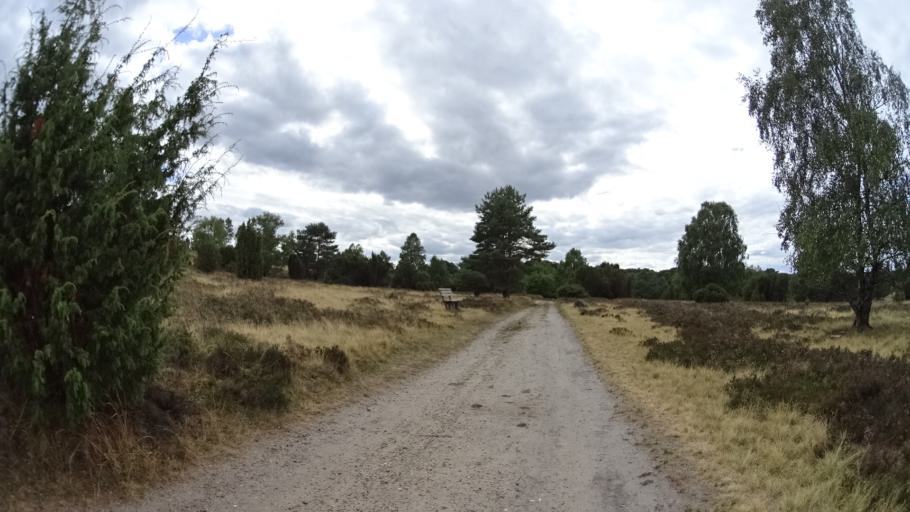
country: DE
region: Lower Saxony
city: Undeloh
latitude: 53.1676
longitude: 9.9766
